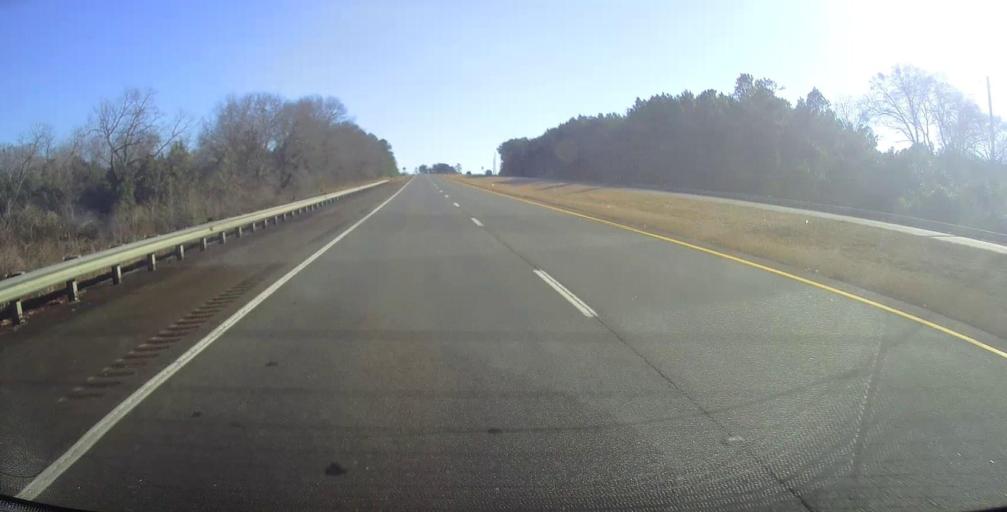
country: US
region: Georgia
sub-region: Sumter County
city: Americus
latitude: 32.0521
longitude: -84.2537
